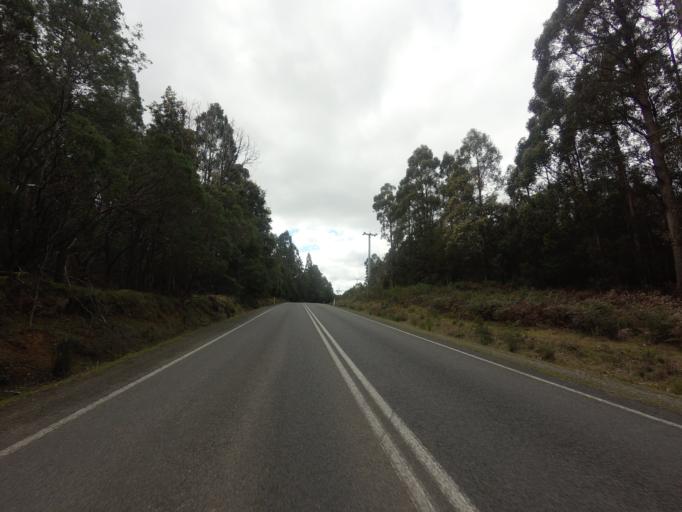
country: AU
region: Tasmania
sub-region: Huon Valley
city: Geeveston
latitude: -43.4001
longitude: 146.9554
